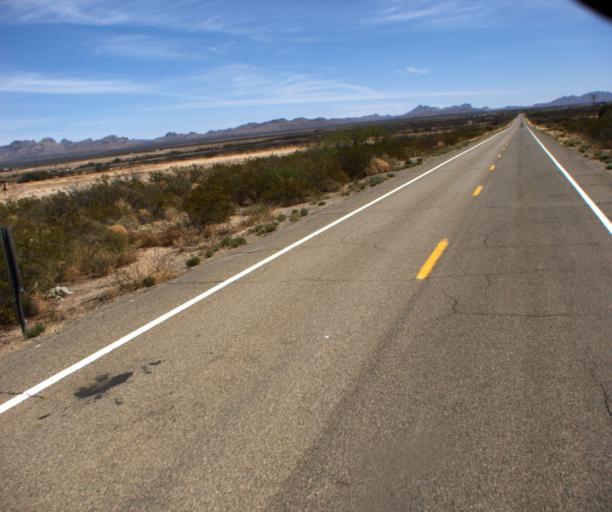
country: US
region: New Mexico
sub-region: Hidalgo County
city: Lordsburg
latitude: 32.2637
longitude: -109.2147
